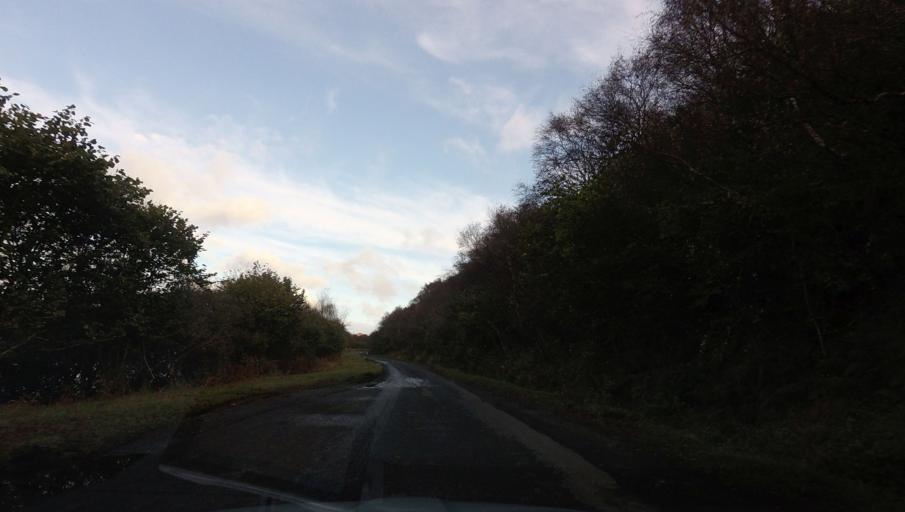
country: GB
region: Scotland
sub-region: Argyll and Bute
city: Isle Of Mull
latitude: 56.3363
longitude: -6.1580
